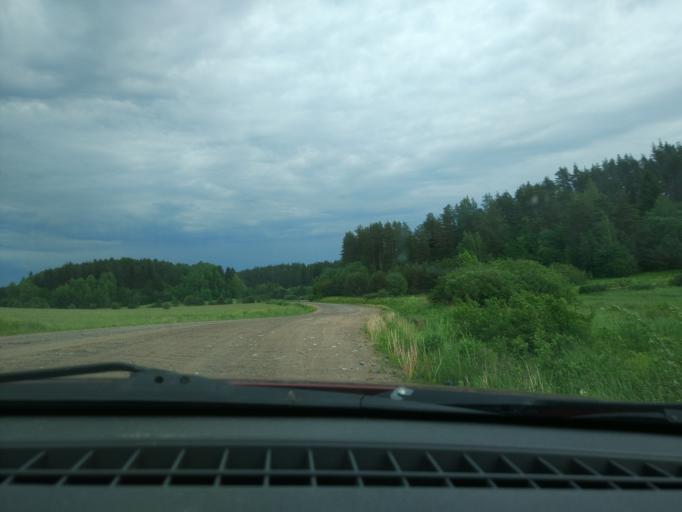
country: RU
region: Leningrad
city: Kuznechnoye
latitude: 61.2798
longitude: 29.8513
